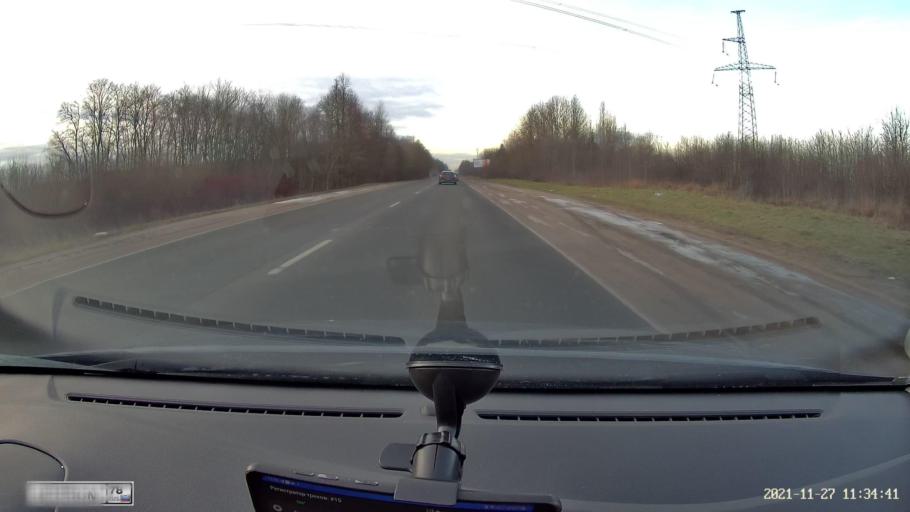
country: RU
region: Leningrad
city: Russko-Vysotskoye
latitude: 59.7055
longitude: 29.9958
